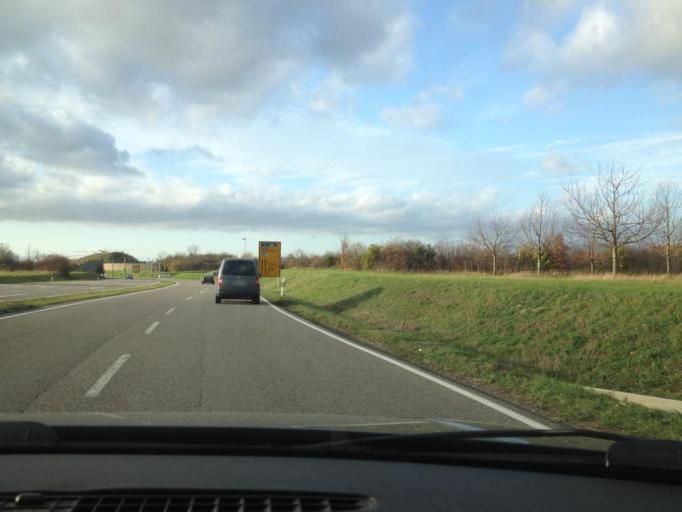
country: DE
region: Baden-Wuerttemberg
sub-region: Karlsruhe Region
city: Walldorf
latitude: 49.2954
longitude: 8.6524
